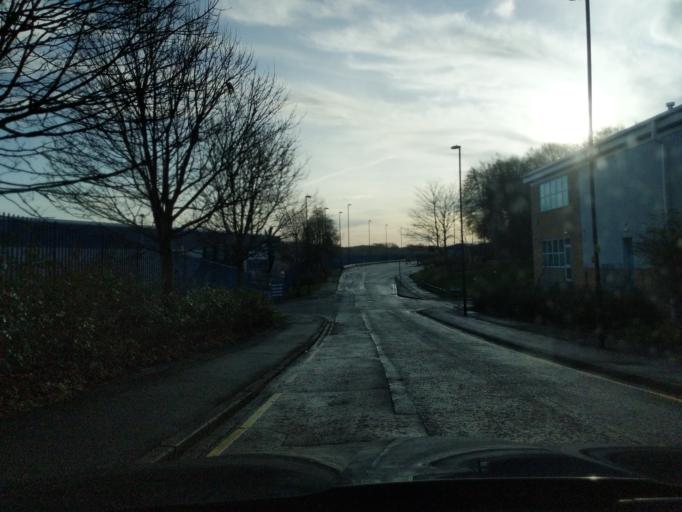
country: GB
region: England
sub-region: Borough of North Tyneside
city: Wallsend
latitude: 54.9785
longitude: -1.5371
